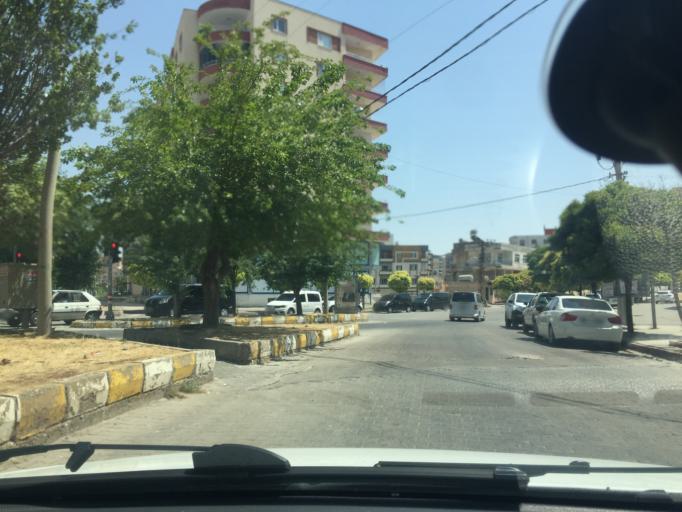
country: TR
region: Mardin
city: Midyat
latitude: 37.4324
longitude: 41.3361
